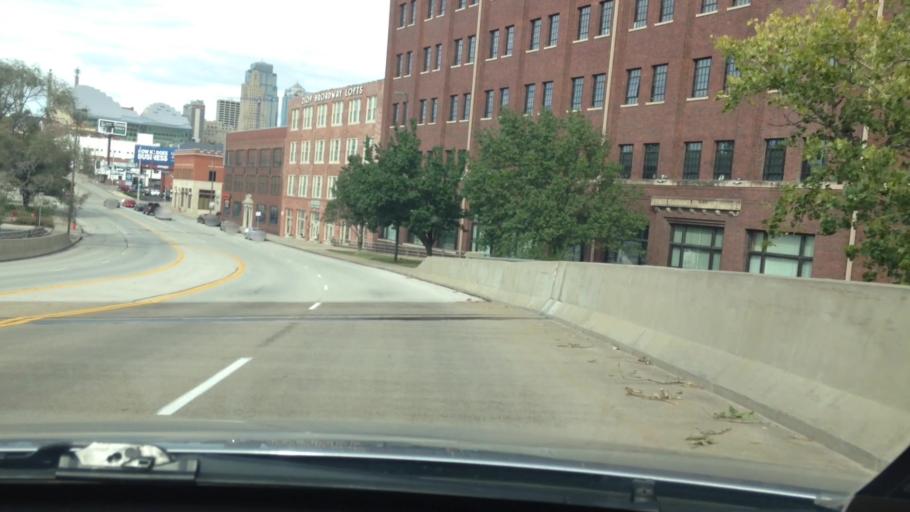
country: US
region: Missouri
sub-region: Jackson County
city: Kansas City
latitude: 39.0860
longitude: -94.5893
